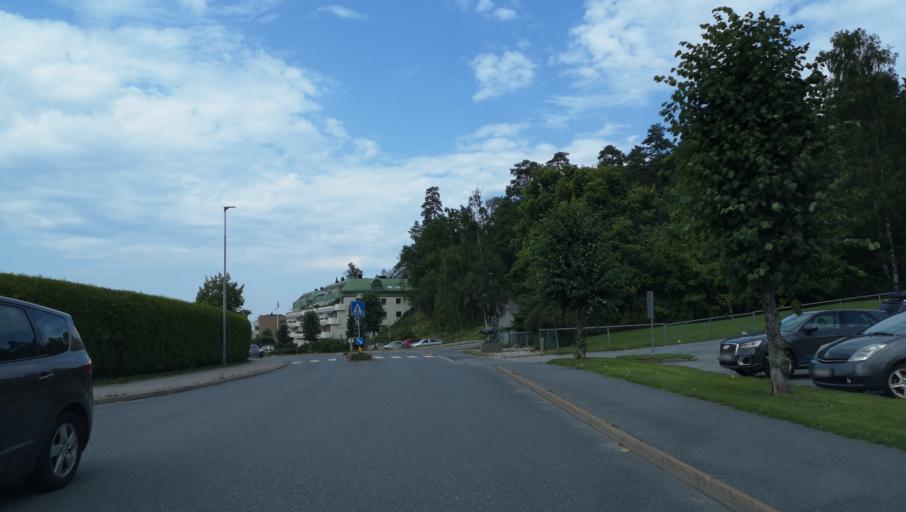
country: NO
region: Ostfold
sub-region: Moss
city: Moss
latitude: 59.4413
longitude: 10.6205
